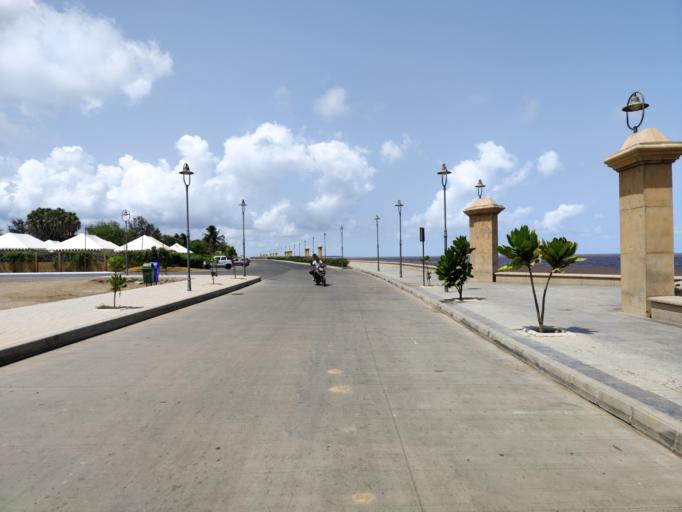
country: IN
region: Daman and Diu
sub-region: Daman District
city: Daman
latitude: 20.4089
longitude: 72.8297
